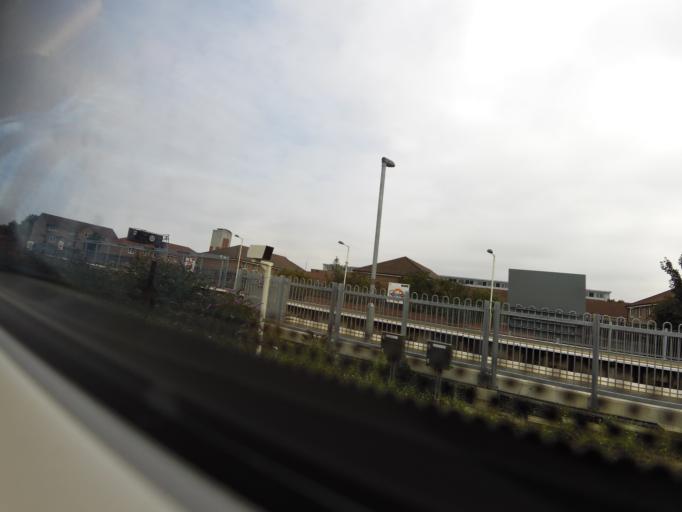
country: GB
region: England
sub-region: Greater London
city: Catford
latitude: 51.4764
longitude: -0.0410
